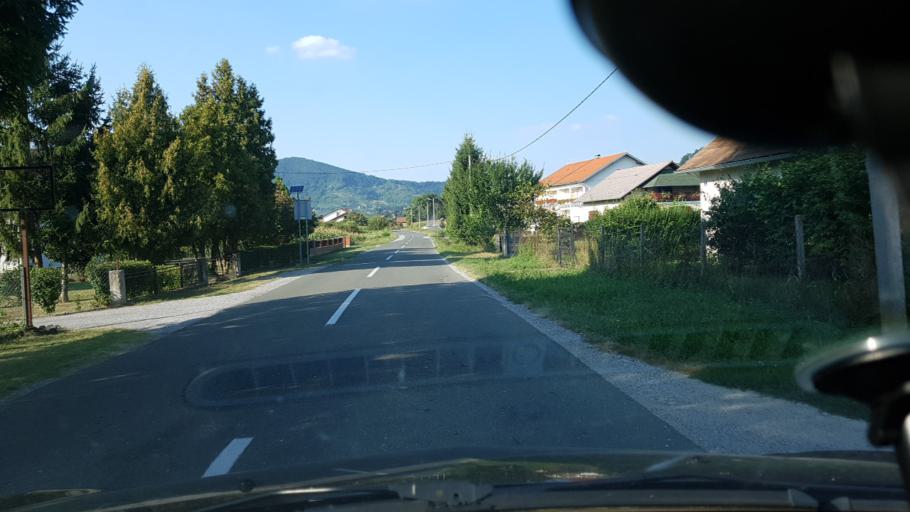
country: SI
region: Bistrica ob Sotli
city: Bistrica ob Sotli
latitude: 46.0263
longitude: 15.7309
